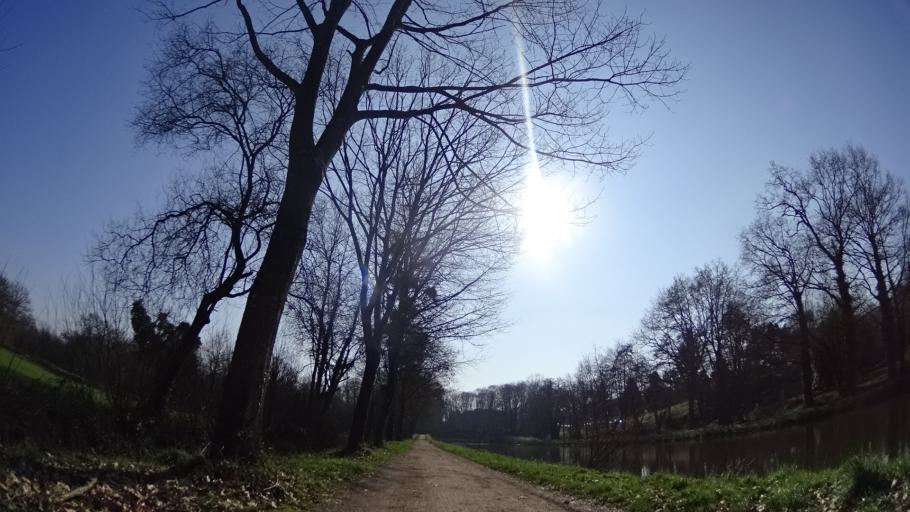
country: FR
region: Brittany
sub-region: Departement d'Ille-et-Vilaine
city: Saint-Gregoire
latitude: 48.1474
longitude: -1.6797
